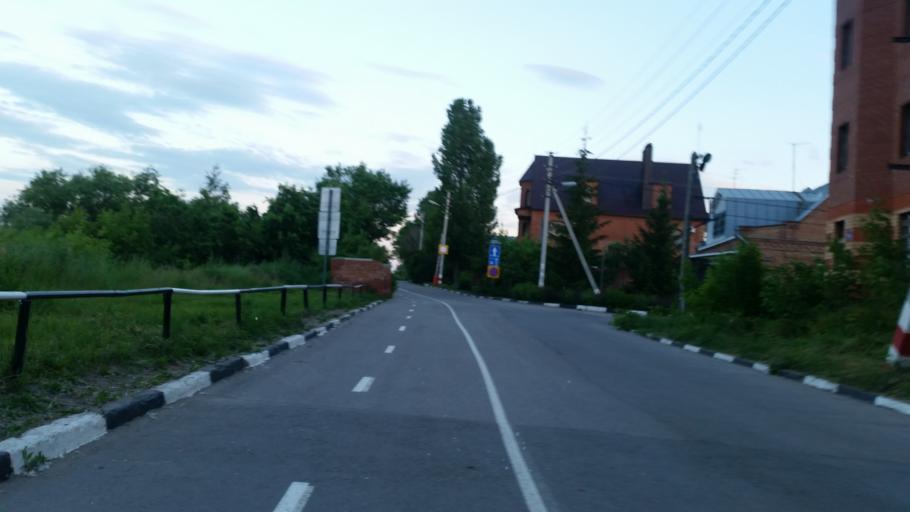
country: RU
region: Ulyanovsk
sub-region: Ulyanovskiy Rayon
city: Ulyanovsk
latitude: 54.3247
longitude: 48.4094
